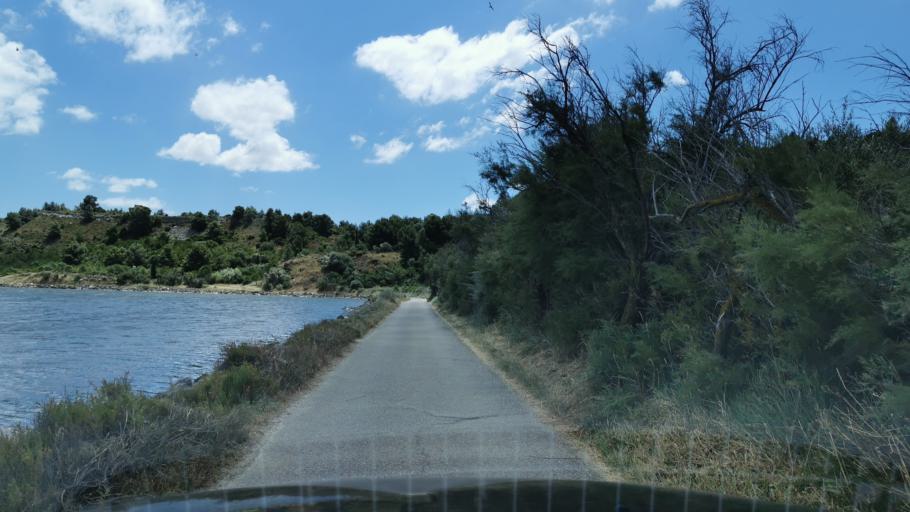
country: FR
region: Languedoc-Roussillon
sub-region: Departement de l'Aude
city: Peyriac-de-Mer
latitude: 43.0879
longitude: 2.9723
